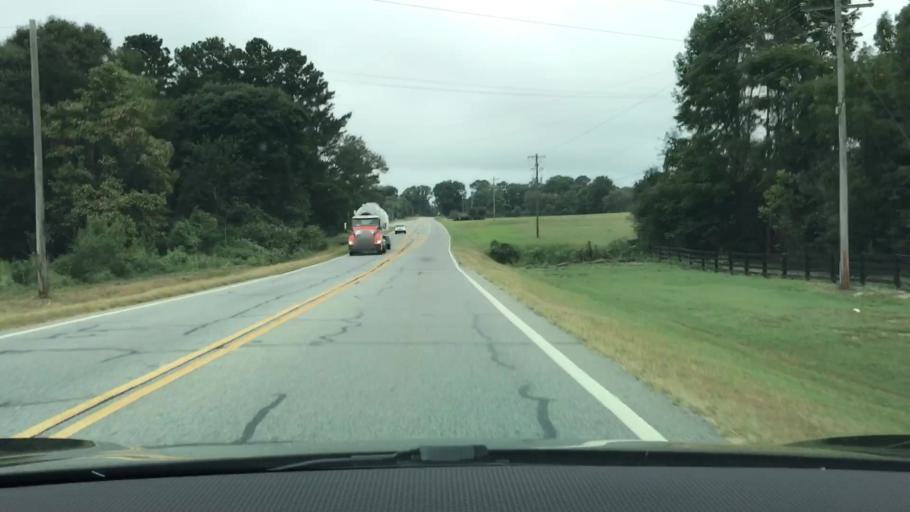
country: US
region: Georgia
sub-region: Oconee County
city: Watkinsville
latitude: 33.8326
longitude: -83.3790
